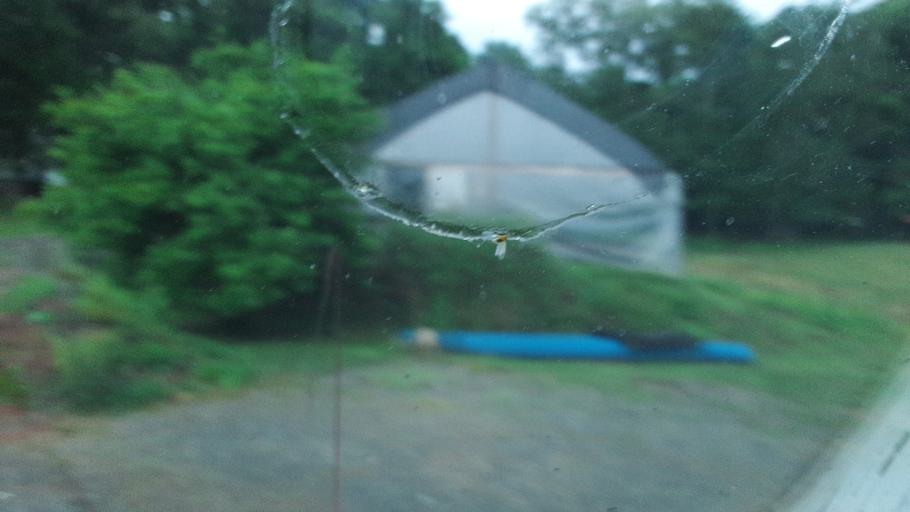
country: US
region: North Carolina
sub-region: Yadkin County
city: Jonesville
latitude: 36.1058
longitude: -80.8990
